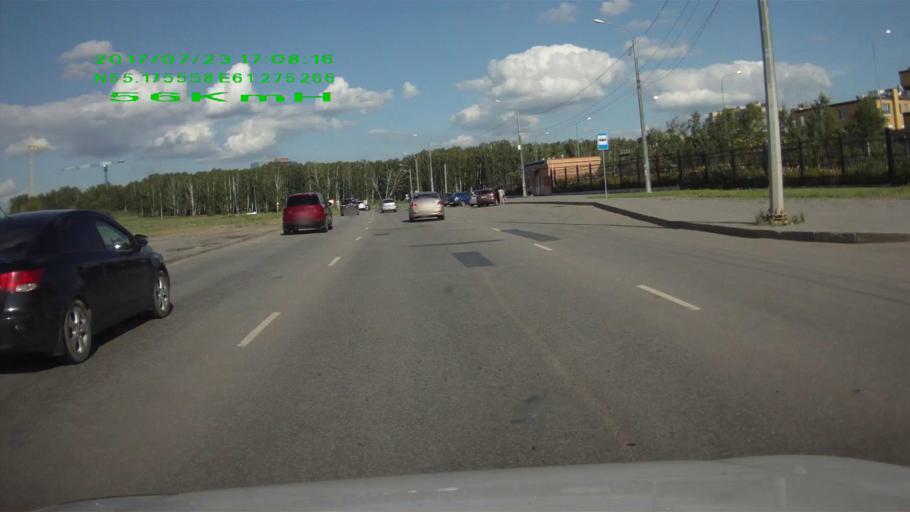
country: RU
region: Chelyabinsk
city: Roshchino
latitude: 55.1753
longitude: 61.2759
